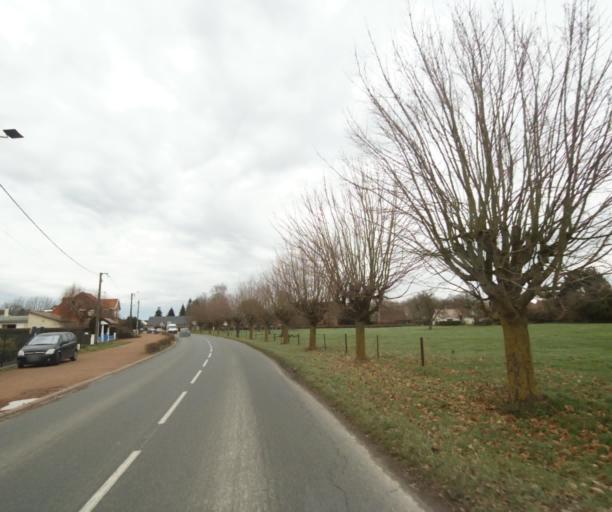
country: FR
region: Nord-Pas-de-Calais
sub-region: Departement du Nord
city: Sebourg
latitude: 50.3431
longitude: 3.6398
